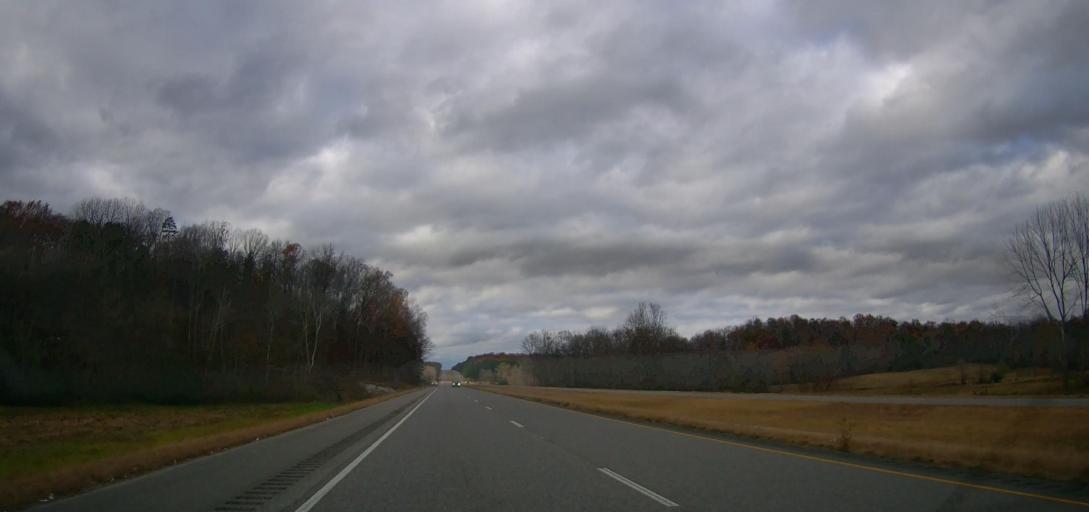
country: US
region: Alabama
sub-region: Lawrence County
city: Town Creek
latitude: 34.6071
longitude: -87.4528
